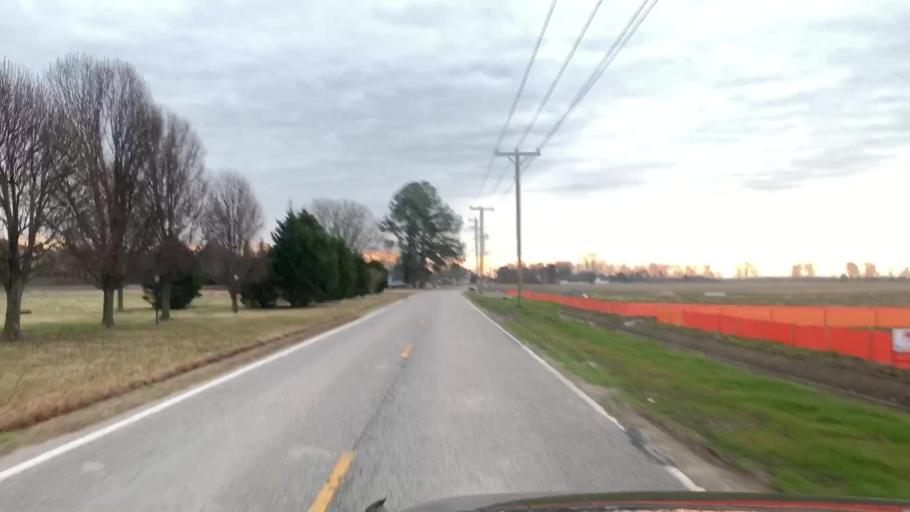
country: US
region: North Carolina
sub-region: Currituck County
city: Moyock
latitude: 36.6286
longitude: -76.1703
